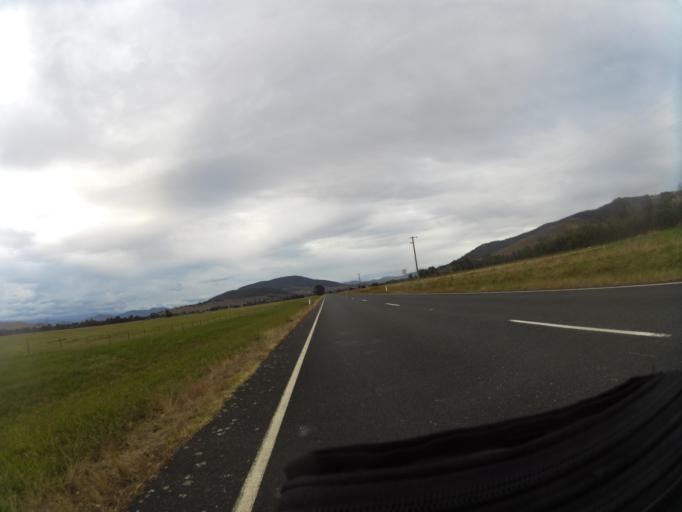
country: AU
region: New South Wales
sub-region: Snowy River
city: Jindabyne
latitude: -36.0970
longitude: 147.9816
